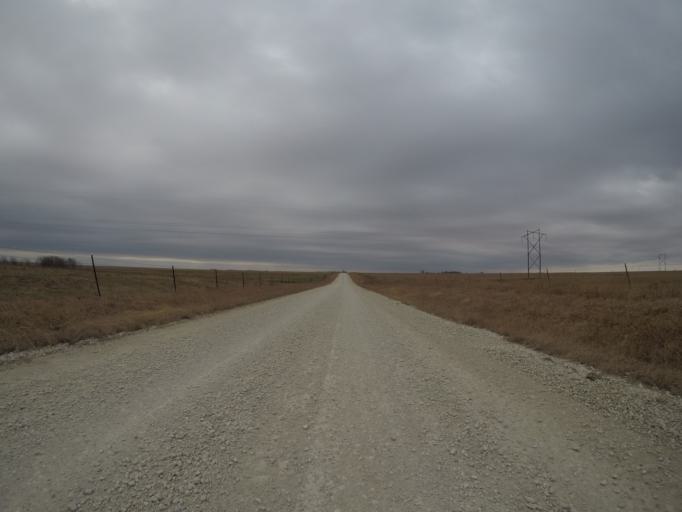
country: US
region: Kansas
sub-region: Wabaunsee County
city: Alma
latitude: 38.7548
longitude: -96.1496
